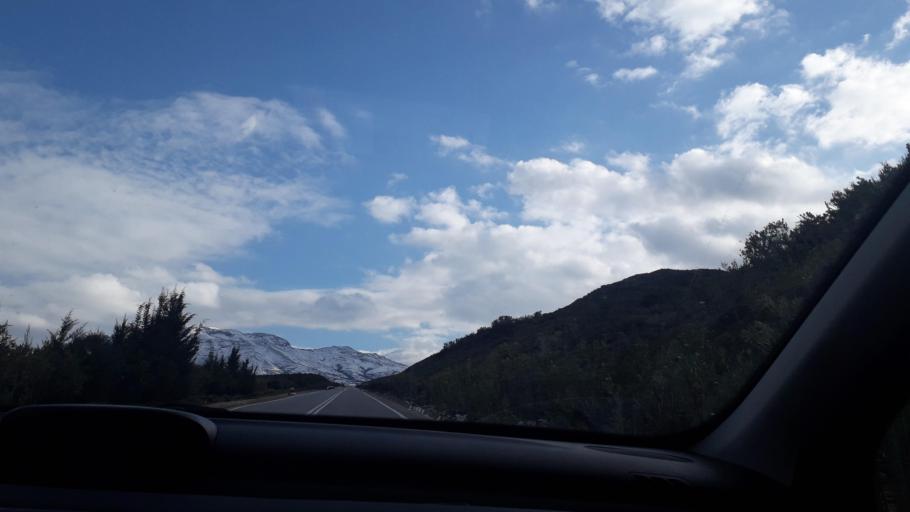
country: GR
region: Crete
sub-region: Nomos Rethymnis
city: Agia Foteini
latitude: 35.2746
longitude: 24.5599
